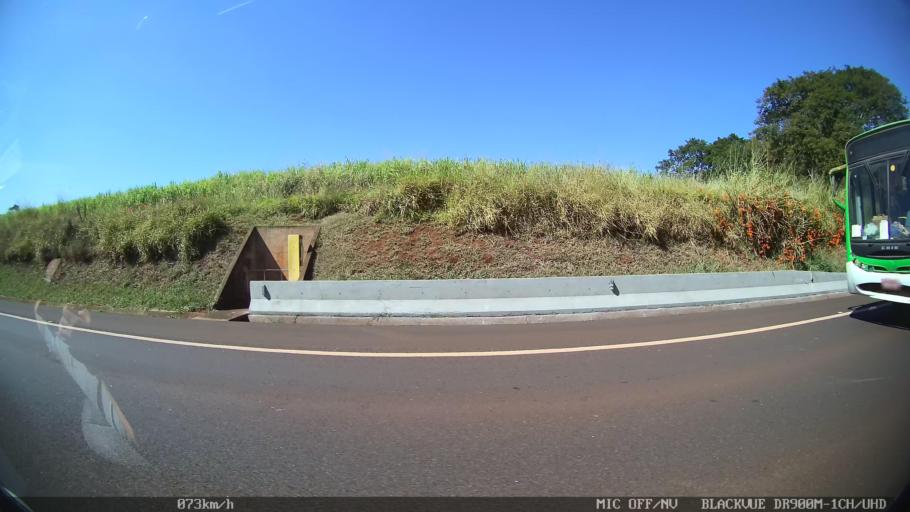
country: BR
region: Sao Paulo
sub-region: Franca
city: Franca
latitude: -20.6313
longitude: -47.4665
